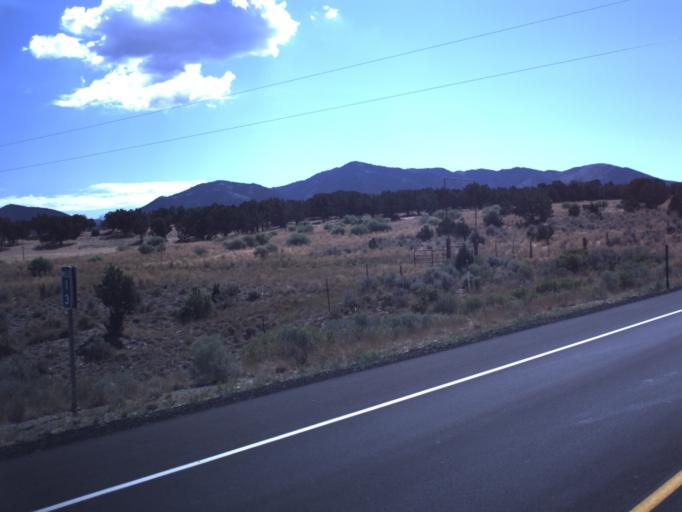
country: US
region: Utah
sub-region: Utah County
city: Eagle Mountain
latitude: 40.0472
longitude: -112.2940
